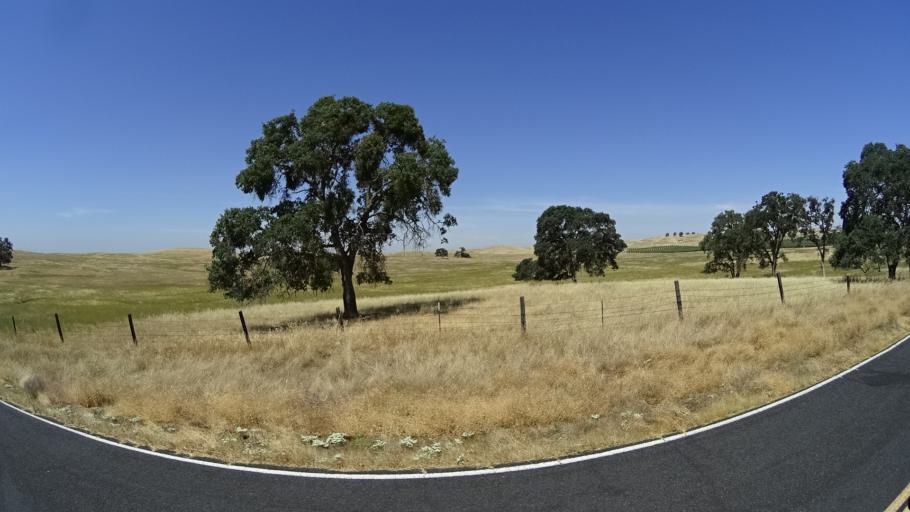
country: US
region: California
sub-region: Calaveras County
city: Rancho Calaveras
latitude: 38.1004
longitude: -120.9446
